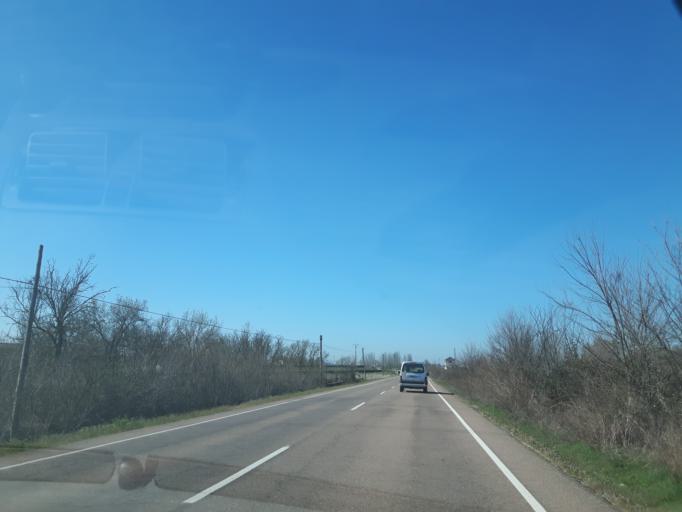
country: ES
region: Castille and Leon
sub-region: Provincia de Salamanca
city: Lumbrales
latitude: 40.9425
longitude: -6.6975
